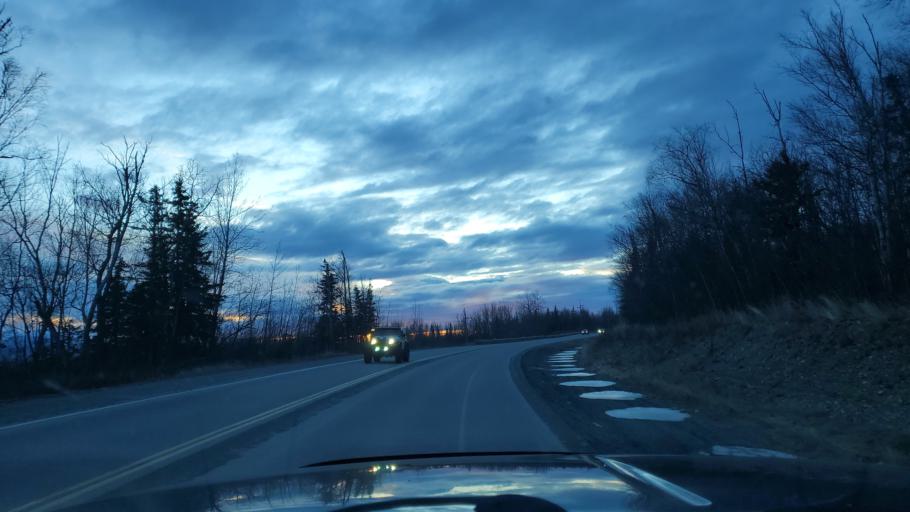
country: US
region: Alaska
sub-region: Matanuska-Susitna Borough
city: Lakes
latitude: 61.6093
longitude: -149.3318
